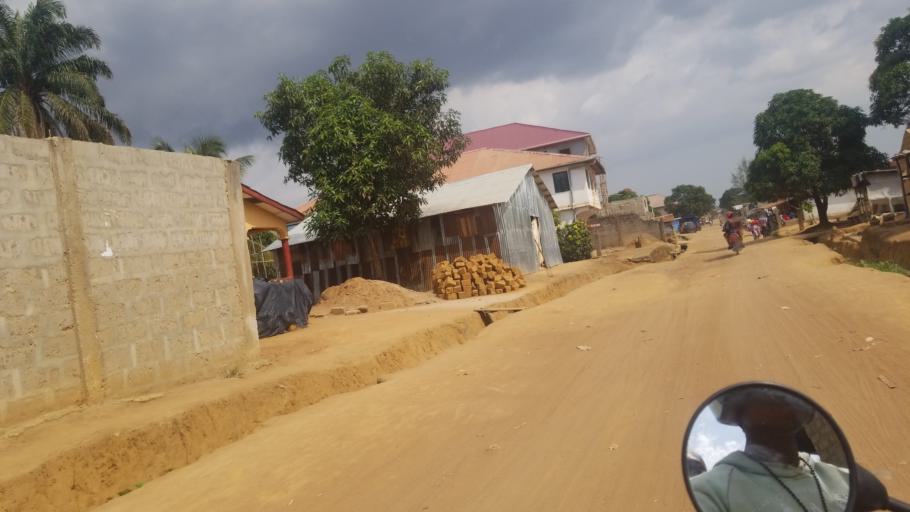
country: SL
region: Western Area
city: Waterloo
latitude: 8.3378
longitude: -13.0493
